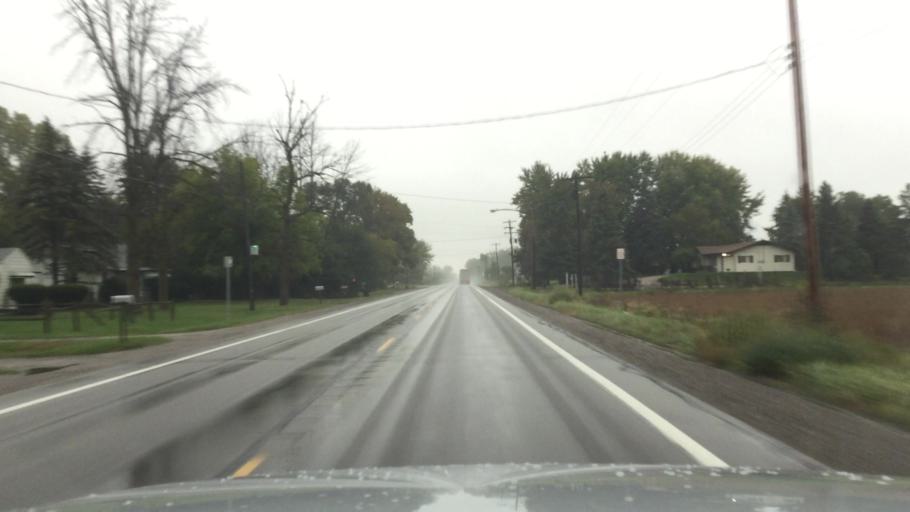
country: US
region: Michigan
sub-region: Saginaw County
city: Saginaw
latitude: 43.3813
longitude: -83.9553
